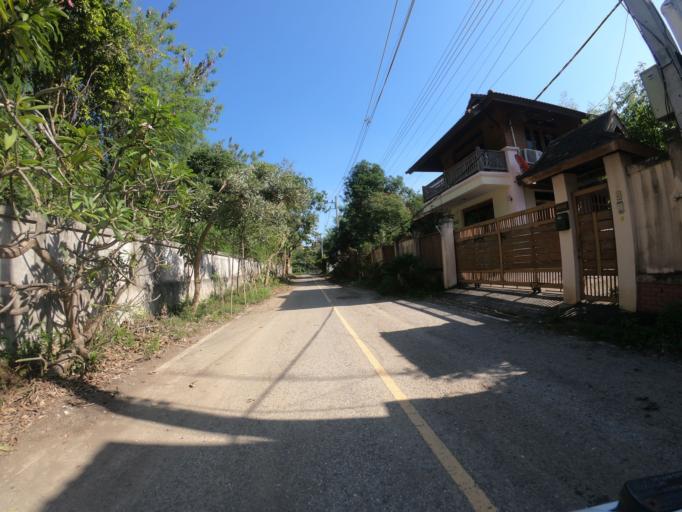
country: TH
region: Chiang Mai
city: Chiang Mai
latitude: 18.7422
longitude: 98.9687
